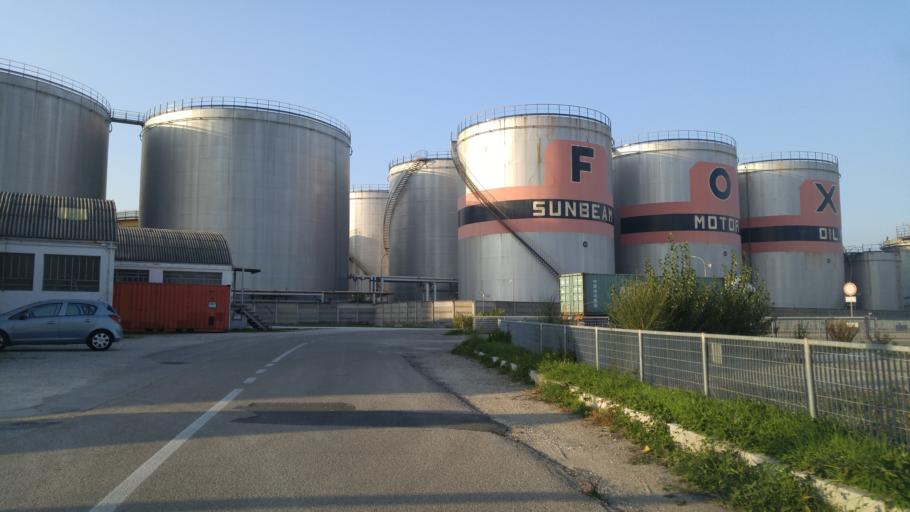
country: IT
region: The Marches
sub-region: Provincia di Pesaro e Urbino
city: Pesaro
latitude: 43.9034
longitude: 12.8846
